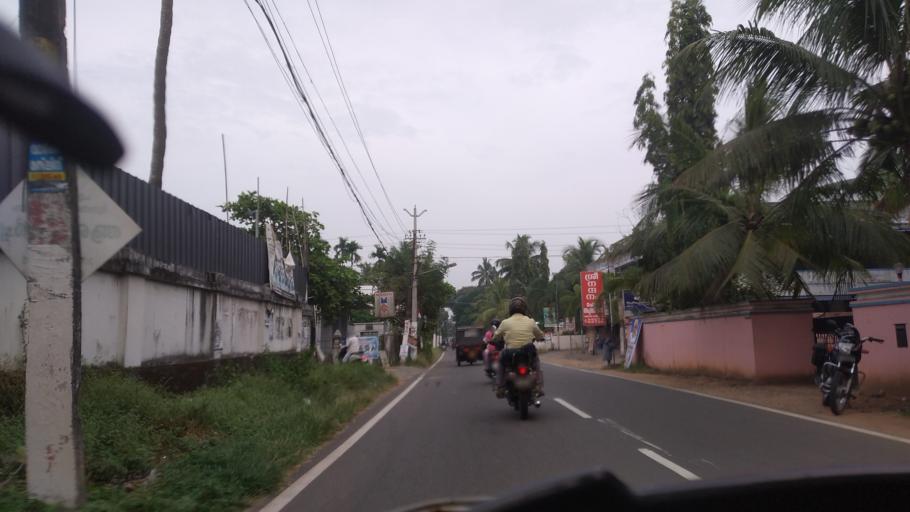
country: IN
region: Kerala
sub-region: Ernakulam
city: Elur
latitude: 10.1499
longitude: 76.2587
